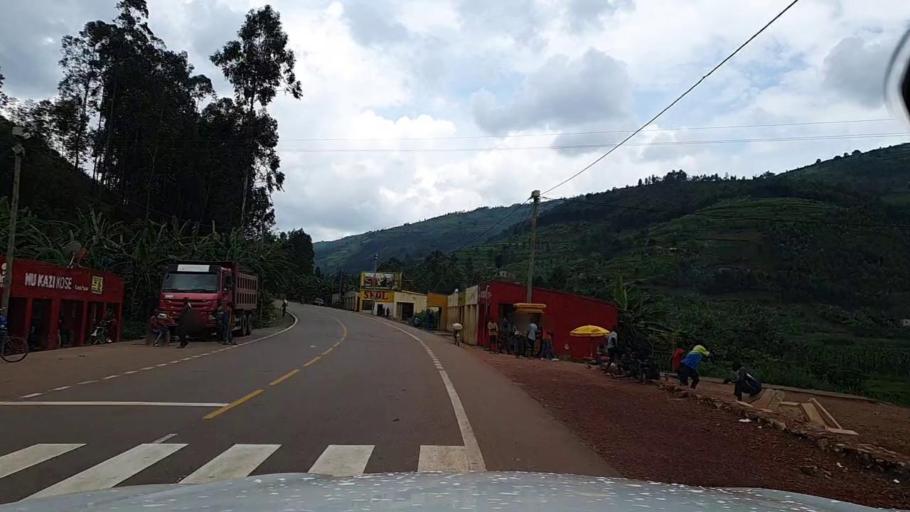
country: RW
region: Northern Province
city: Byumba
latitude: -1.7124
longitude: 30.1240
